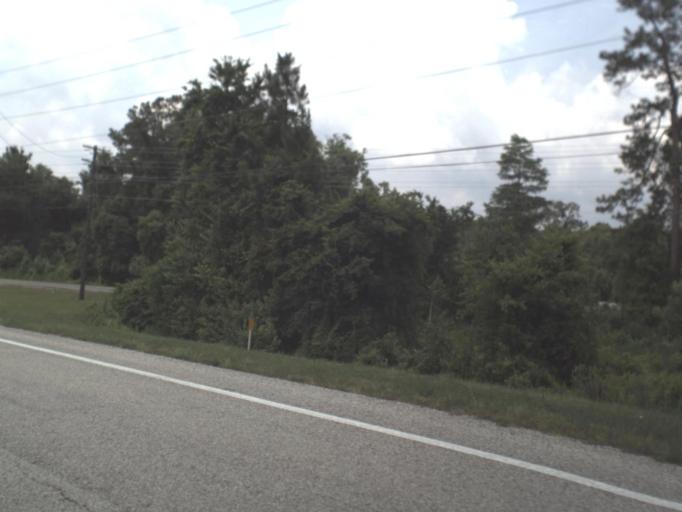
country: US
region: Florida
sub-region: Clay County
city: Green Cove Springs
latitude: 29.9350
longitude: -81.6886
